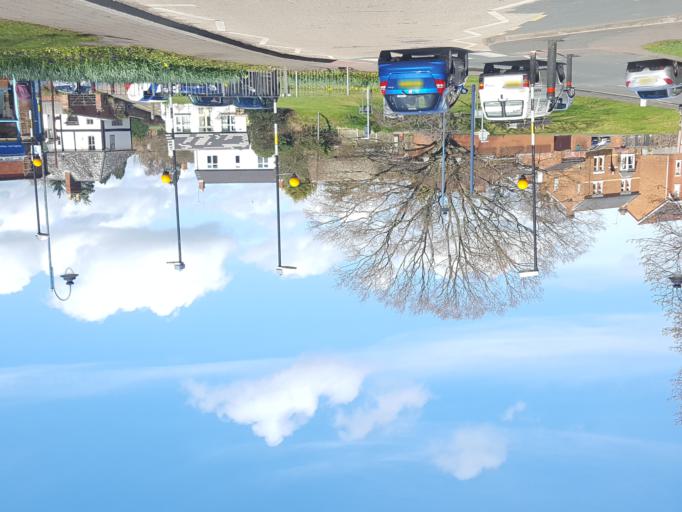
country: GB
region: England
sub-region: Worcestershire
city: Great Malvern
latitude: 52.1086
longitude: -2.3121
